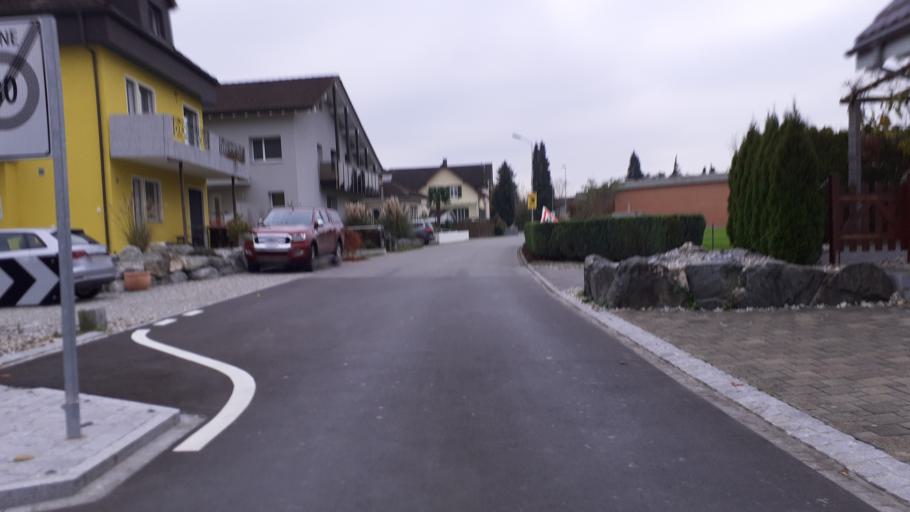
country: CH
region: Appenzell Innerrhoden
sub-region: Appenzell Inner Rhodes
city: Balgach
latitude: 47.4069
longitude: 9.6278
